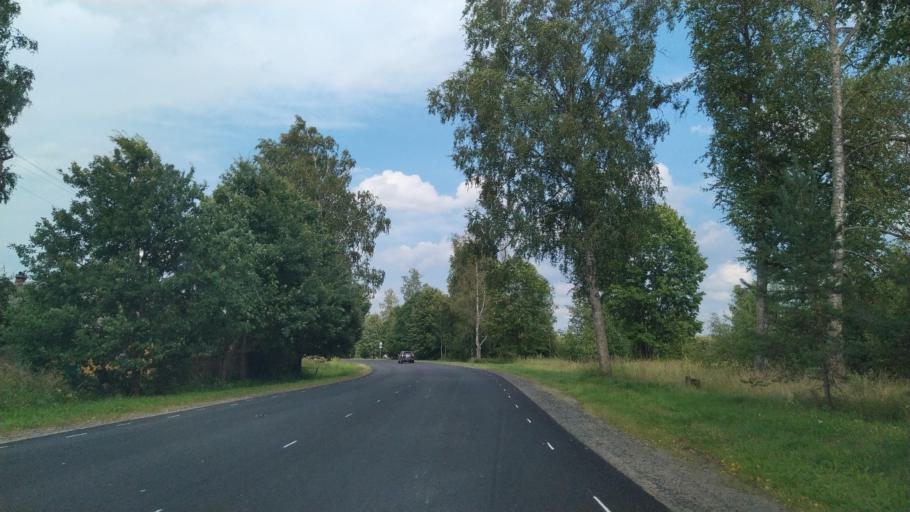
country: RU
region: Pskov
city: Porkhov
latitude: 57.8304
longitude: 29.5309
